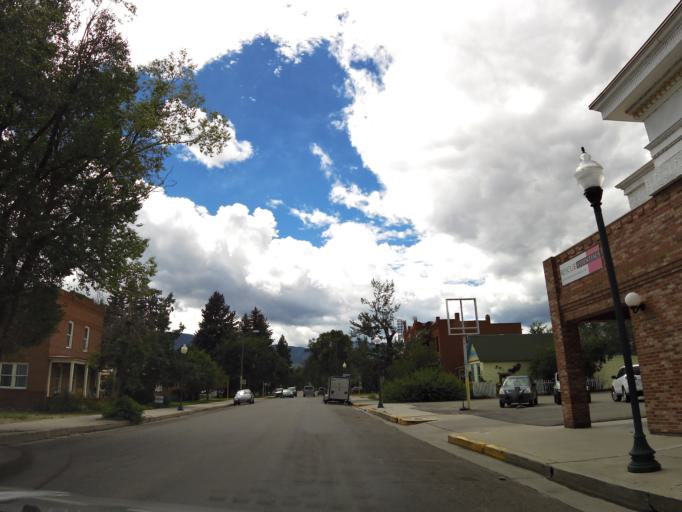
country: US
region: Colorado
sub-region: Chaffee County
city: Salida
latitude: 38.5344
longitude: -105.9937
